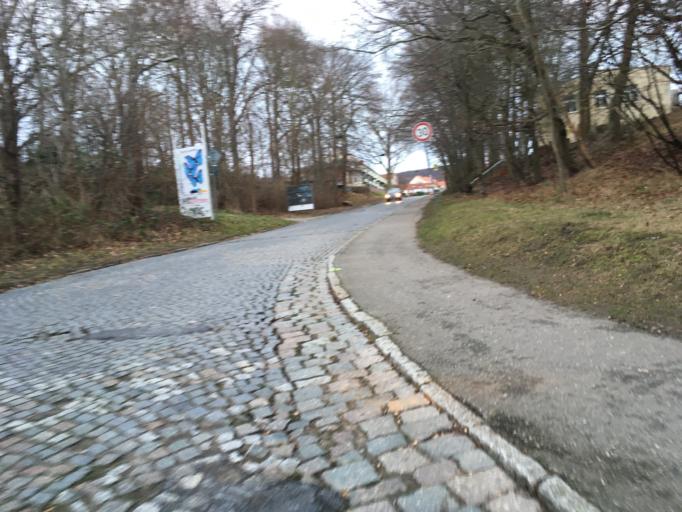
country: DE
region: Mecklenburg-Vorpommern
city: Sassnitz
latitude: 54.5088
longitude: 13.6259
